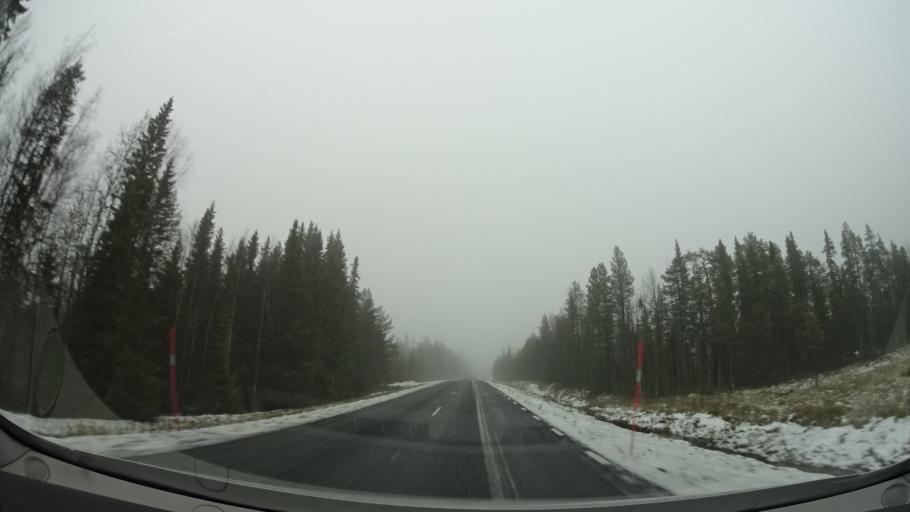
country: SE
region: Vaesterbotten
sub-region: Asele Kommun
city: Insjon
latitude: 64.3135
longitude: 17.6983
